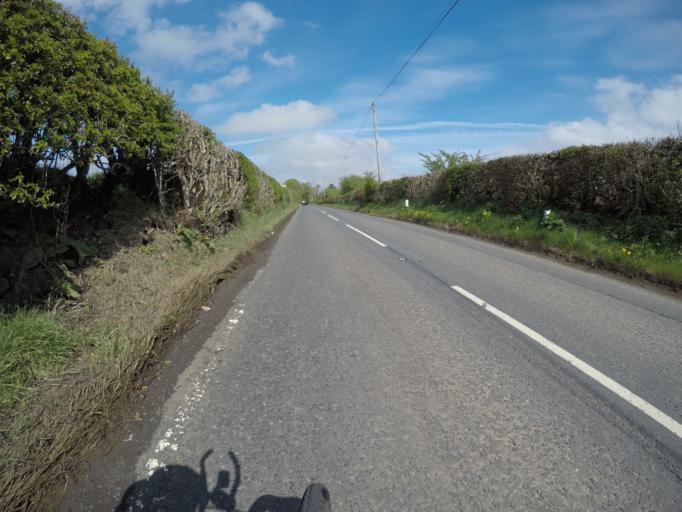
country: GB
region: Scotland
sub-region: East Ayrshire
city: Stewarton
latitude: 55.6922
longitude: -4.4931
